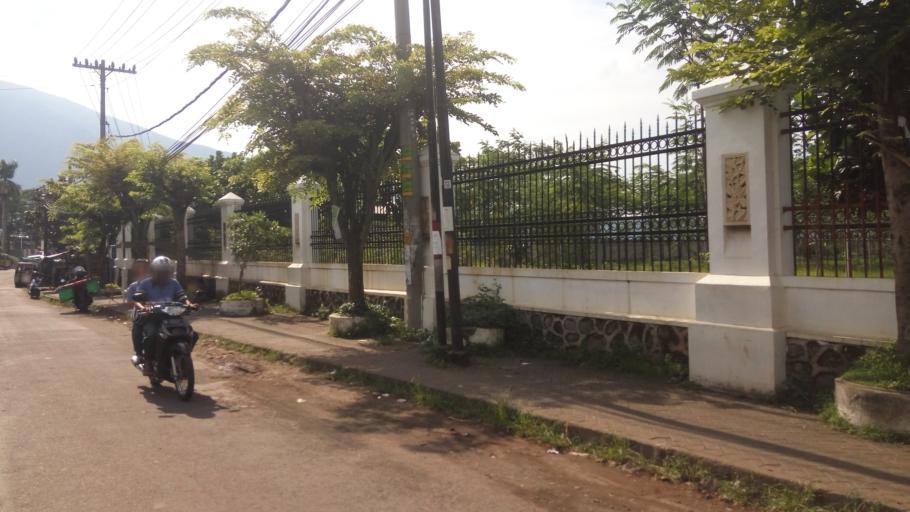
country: ID
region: Central Java
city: Ungaran
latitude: -7.1519
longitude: 110.4153
